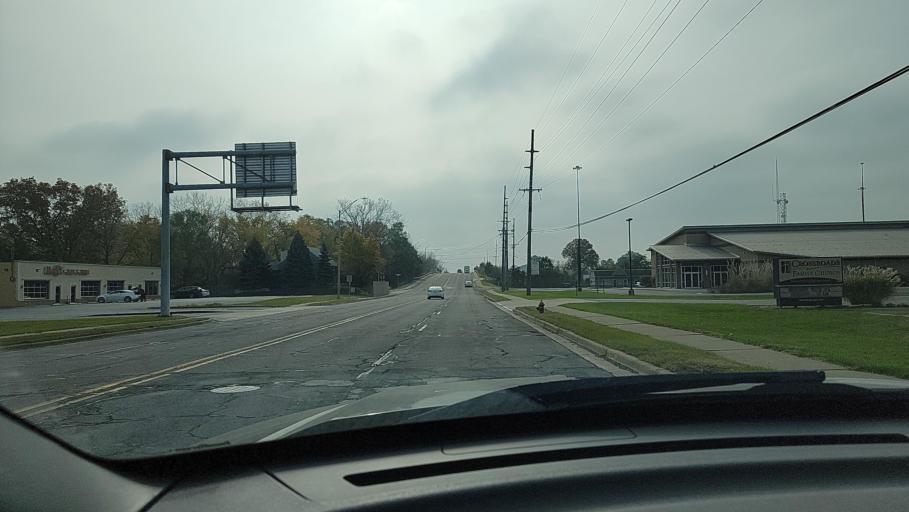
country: US
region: Indiana
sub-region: Porter County
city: Portage
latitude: 41.5833
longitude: -87.1833
